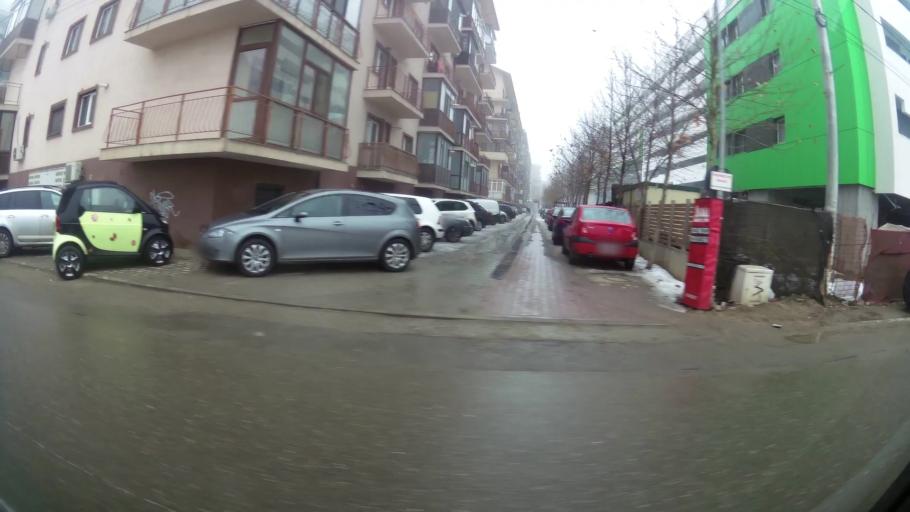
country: RO
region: Ilfov
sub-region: Comuna Chiajna
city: Chiajna
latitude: 44.4420
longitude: 25.9840
